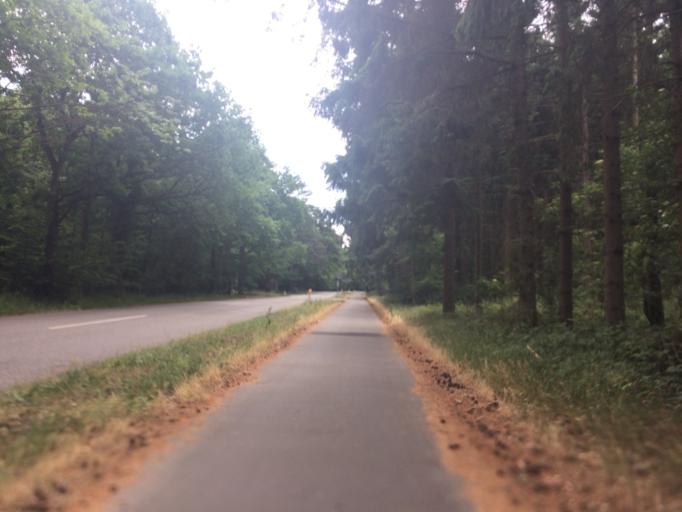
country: DK
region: Capital Region
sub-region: Bornholm Kommune
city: Ronne
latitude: 55.1617
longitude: 14.7156
